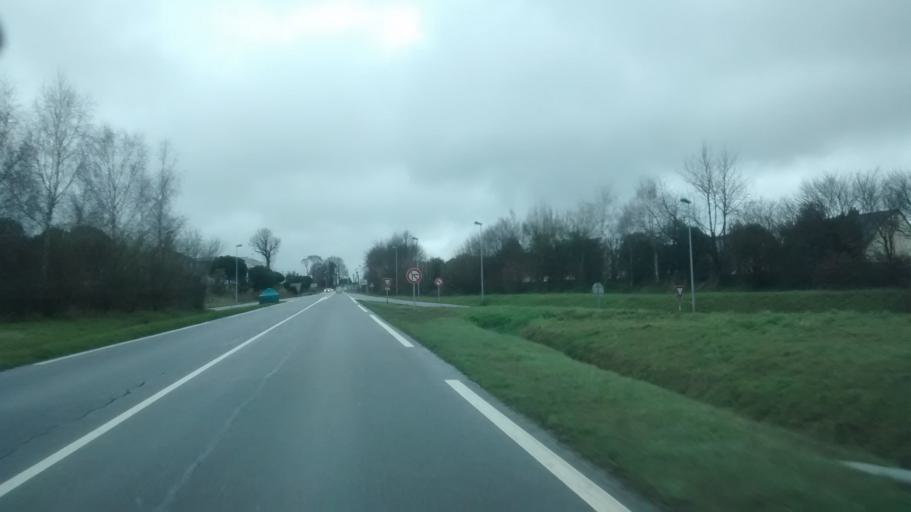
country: FR
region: Brittany
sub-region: Departement d'Ille-et-Vilaine
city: Melesse
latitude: 48.2131
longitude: -1.7008
